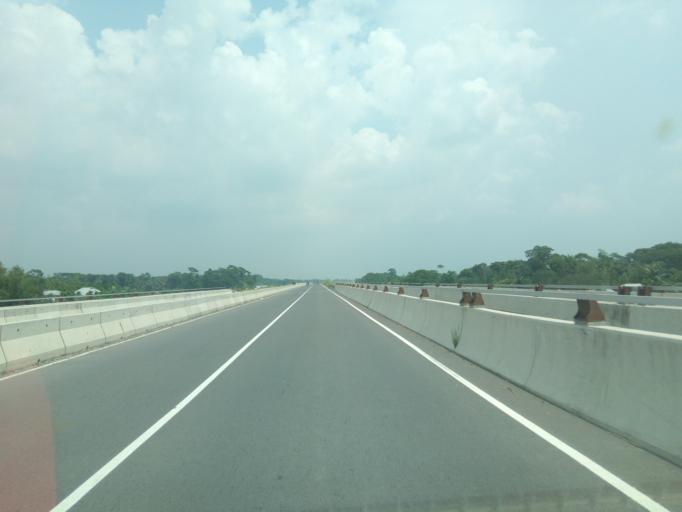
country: BD
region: Dhaka
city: Char Bhadrasan
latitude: 23.3995
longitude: 90.1972
